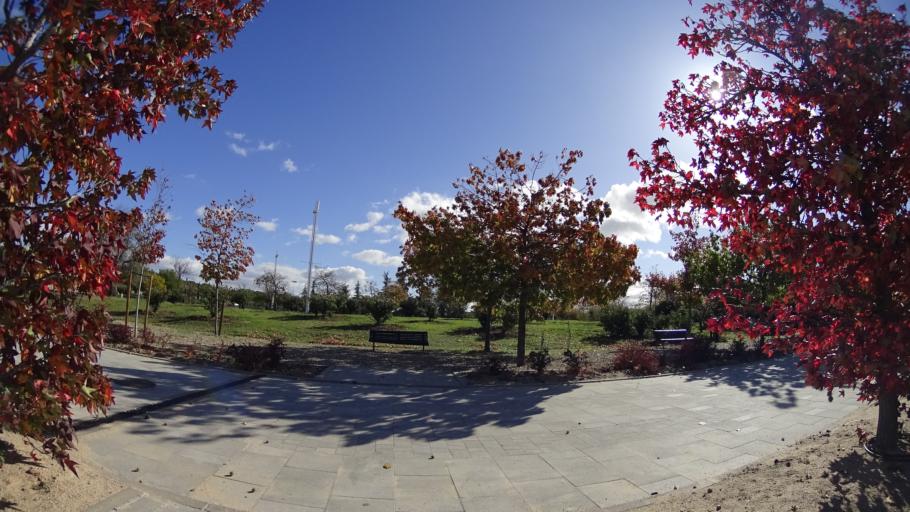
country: ES
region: Madrid
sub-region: Provincia de Madrid
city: San Blas
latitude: 40.4632
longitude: -3.6094
